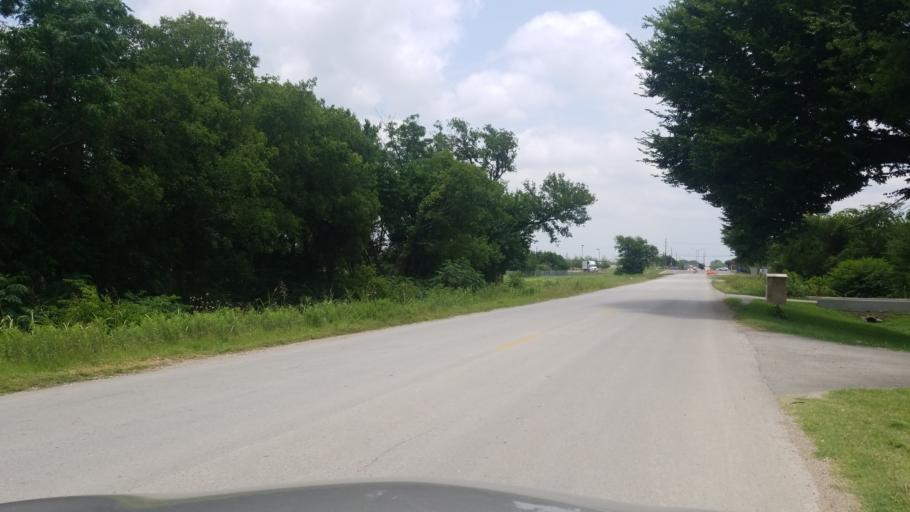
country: US
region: Texas
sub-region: Dallas County
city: Duncanville
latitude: 32.6911
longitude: -96.9124
